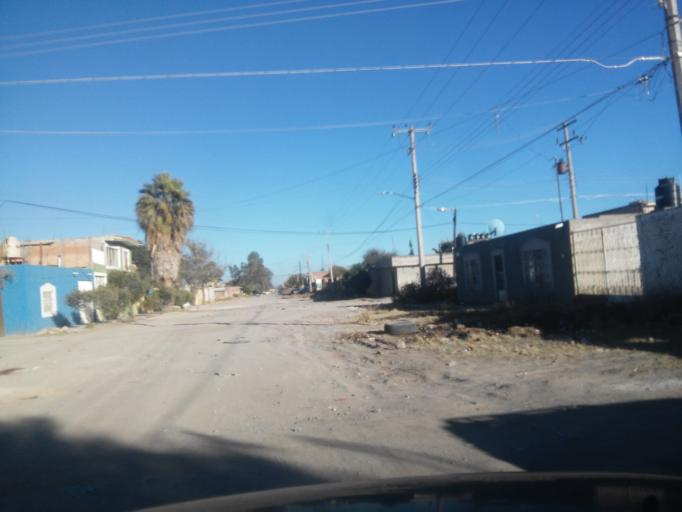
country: MX
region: Durango
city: Victoria de Durango
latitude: 24.0151
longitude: -104.6358
